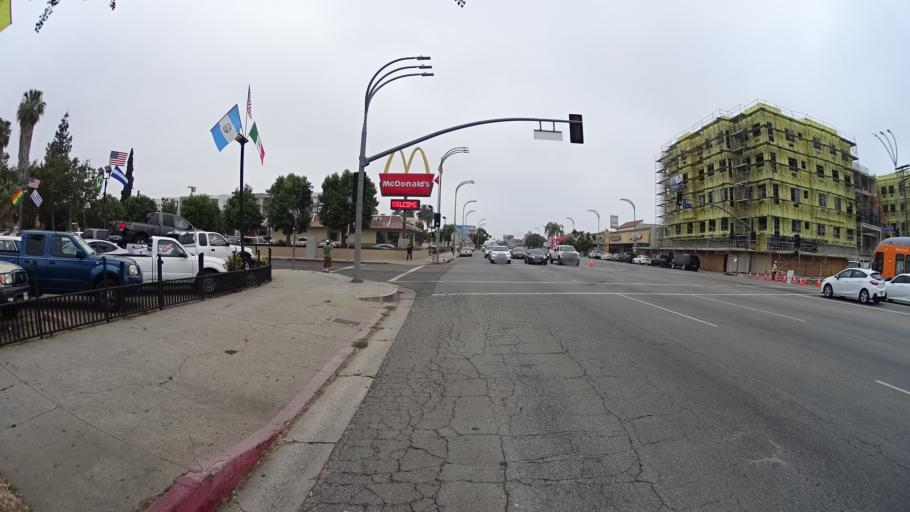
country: US
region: California
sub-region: Los Angeles County
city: Van Nuys
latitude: 34.1982
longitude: -118.4489
